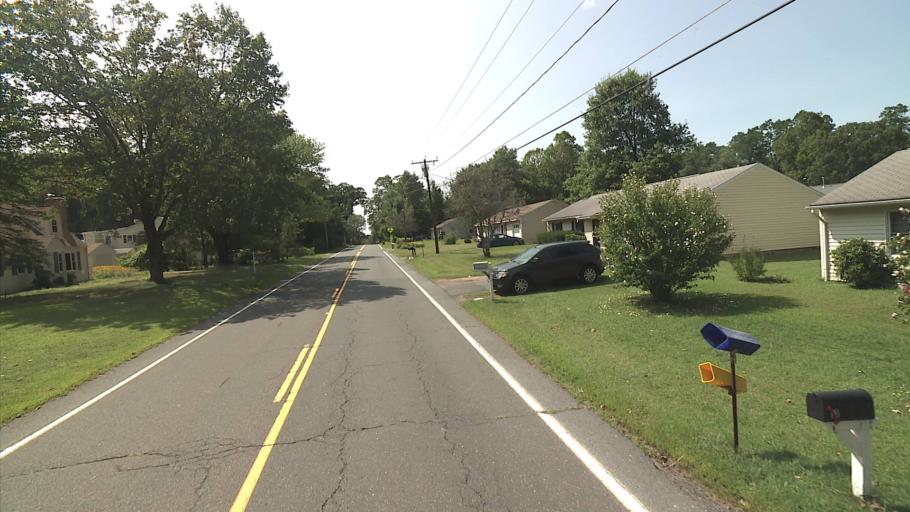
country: US
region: Connecticut
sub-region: Hartford County
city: Windsor Locks
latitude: 41.8941
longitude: -72.6017
